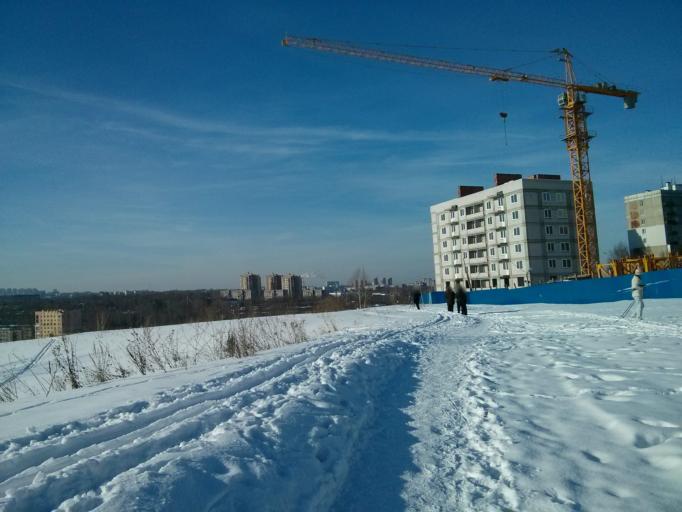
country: RU
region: Nizjnij Novgorod
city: Afonino
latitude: 56.2922
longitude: 44.0619
